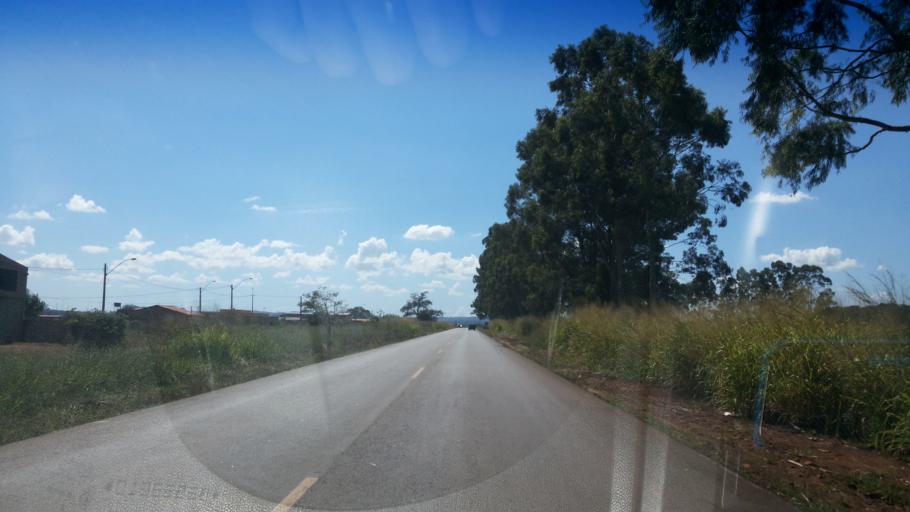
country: BR
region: Goias
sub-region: Goiania
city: Goiania
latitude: -16.5403
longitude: -49.2654
